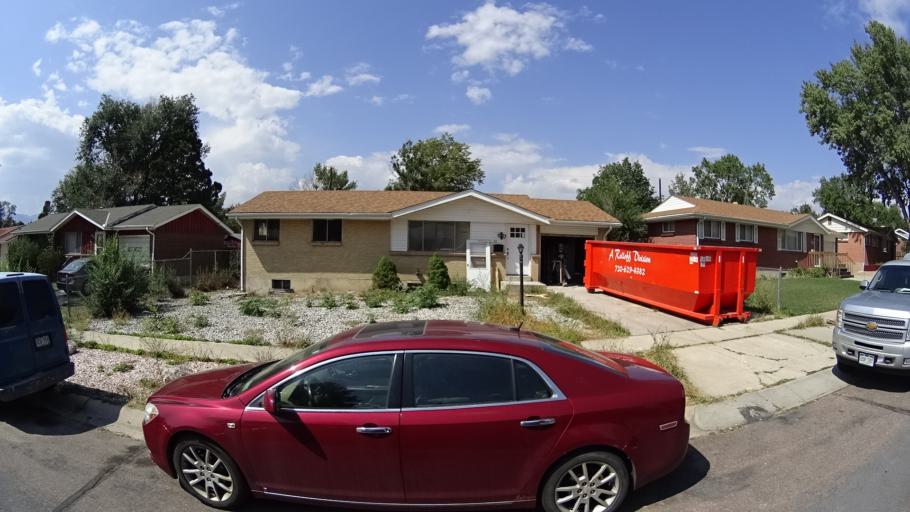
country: US
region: Colorado
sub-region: El Paso County
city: Colorado Springs
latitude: 38.8311
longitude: -104.7674
